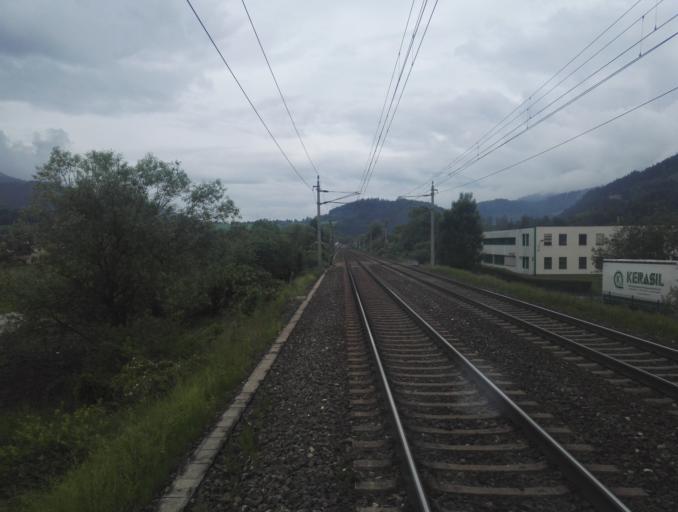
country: AT
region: Styria
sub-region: Politischer Bezirk Bruck-Muerzzuschlag
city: Mitterdorf im Muerztal
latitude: 47.5315
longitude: 15.4982
